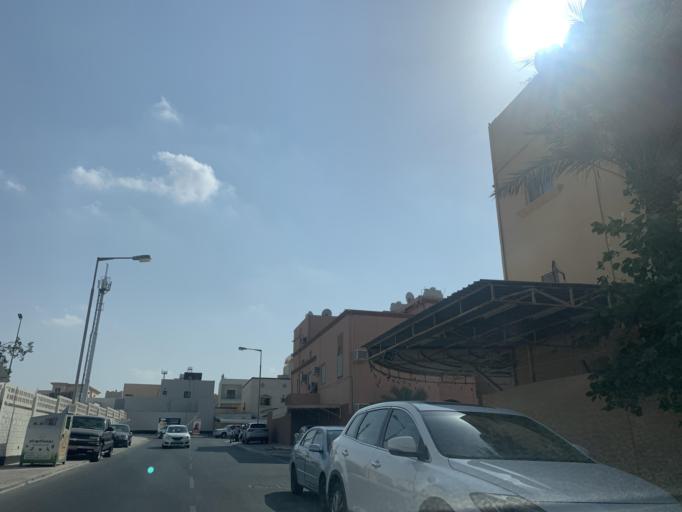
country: BH
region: Central Governorate
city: Madinat Hamad
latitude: 26.1351
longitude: 50.5036
